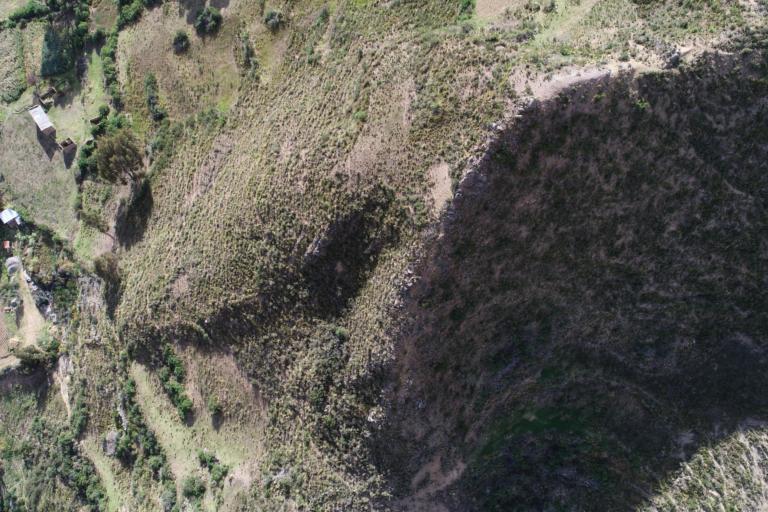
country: BO
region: La Paz
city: La Paz
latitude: -16.5509
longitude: -67.9891
